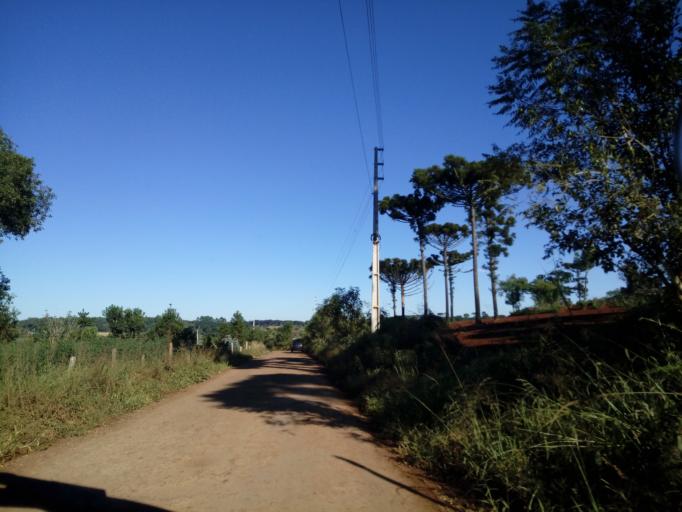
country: BR
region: Santa Catarina
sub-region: Chapeco
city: Chapeco
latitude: -27.1954
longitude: -52.6721
